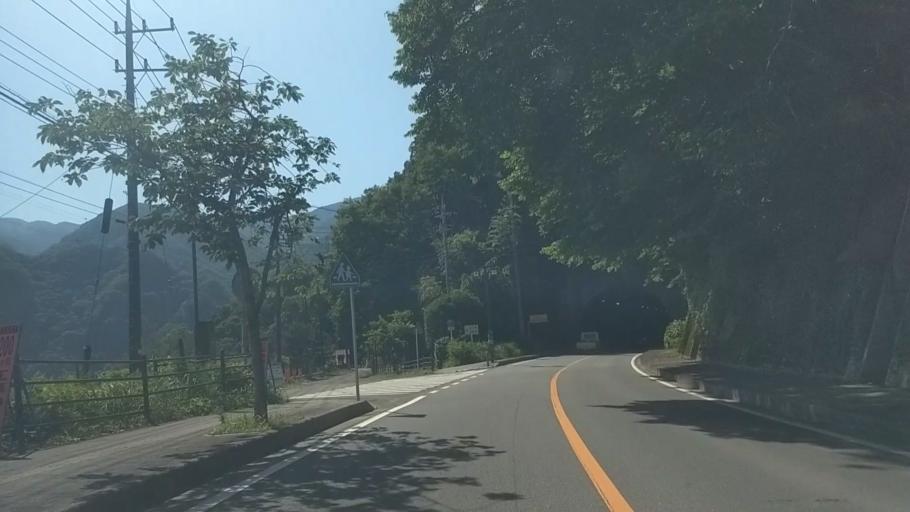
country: JP
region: Shizuoka
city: Fujinomiya
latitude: 35.3688
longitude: 138.4467
